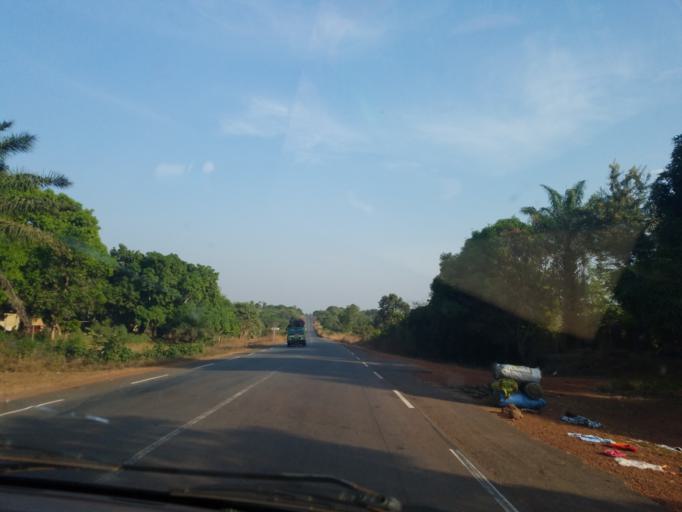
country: GN
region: Boke
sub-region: Boke Prefecture
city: Sangueya
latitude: 10.3763
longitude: -14.3106
